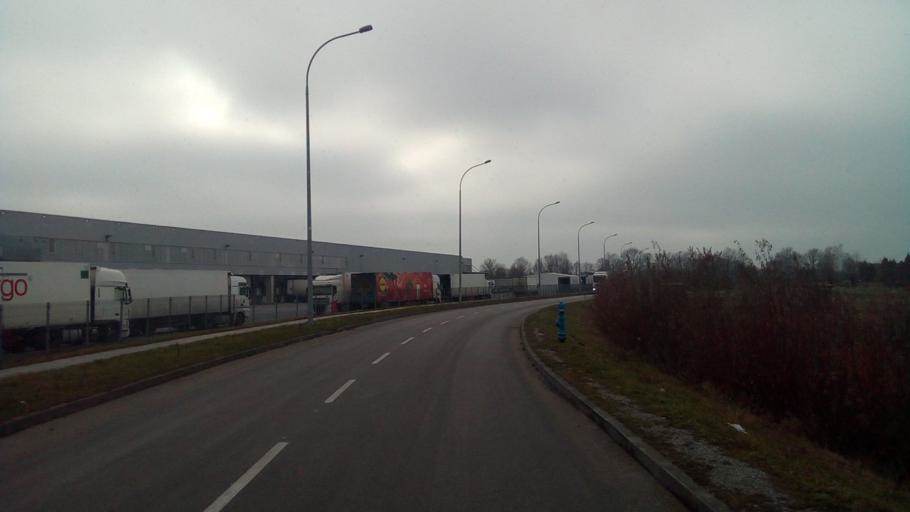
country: HR
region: Zagrebacka
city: Jastrebarsko
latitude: 45.6492
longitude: 15.6750
